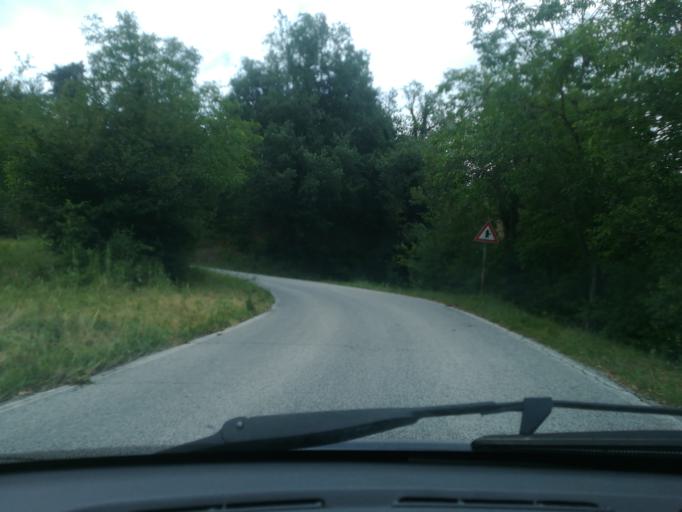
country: IT
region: The Marches
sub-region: Province of Fermo
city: Montefortino
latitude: 42.9400
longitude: 13.3727
